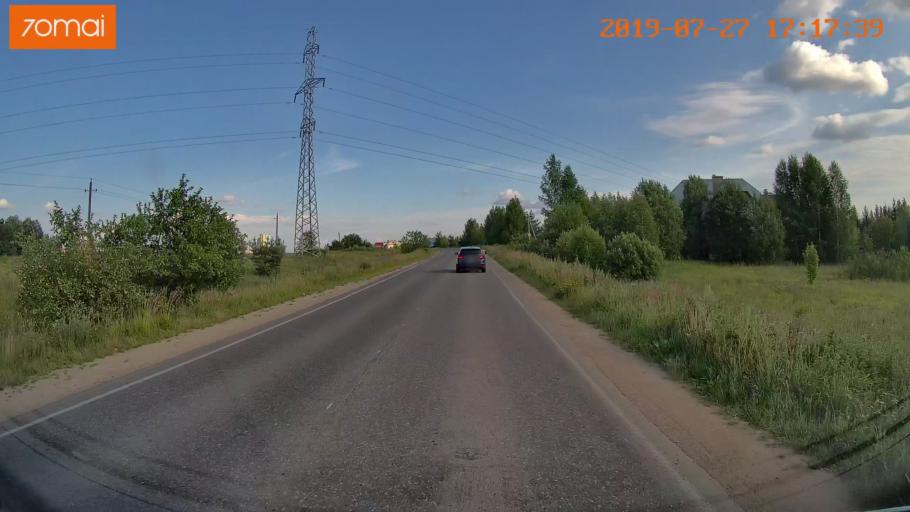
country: RU
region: Ivanovo
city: Novo-Talitsy
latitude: 57.0354
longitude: 40.8971
